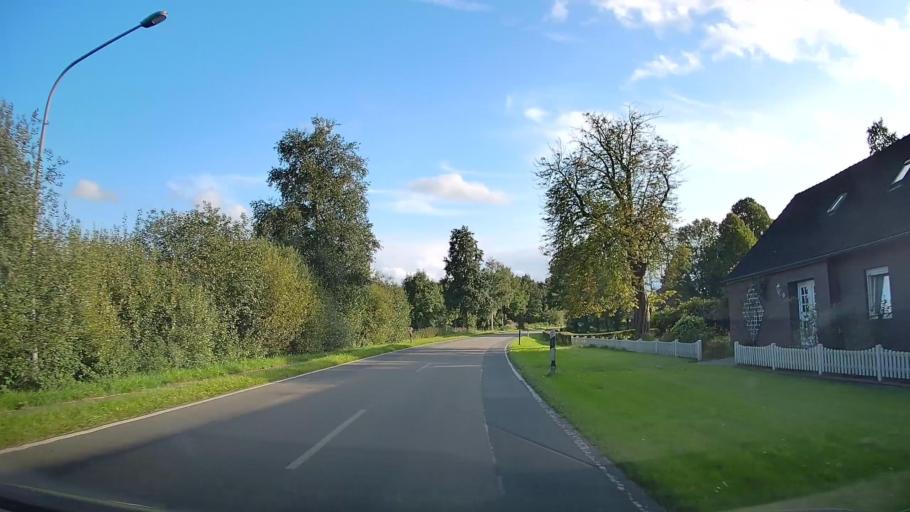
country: DE
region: Lower Saxony
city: Ostrhauderfehn
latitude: 53.1342
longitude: 7.6676
